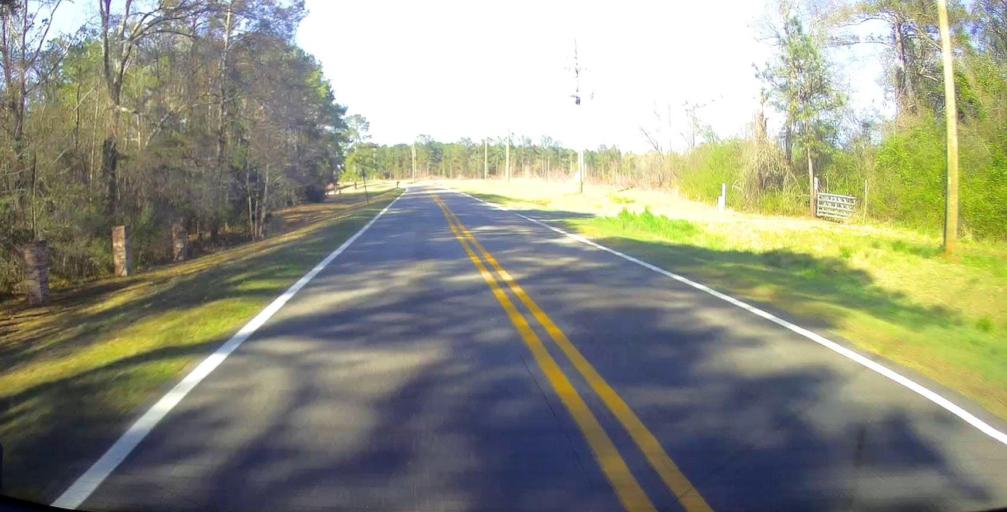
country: US
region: Georgia
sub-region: Peach County
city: Fort Valley
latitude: 32.5850
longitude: -83.9901
